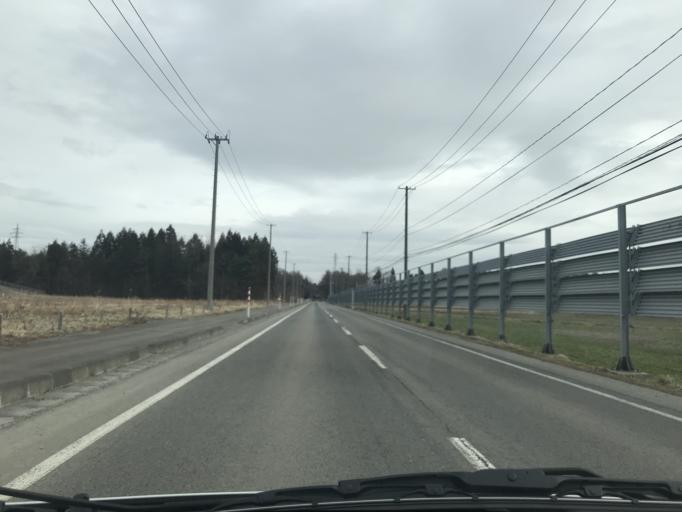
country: JP
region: Iwate
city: Kitakami
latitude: 39.3231
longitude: 141.0067
